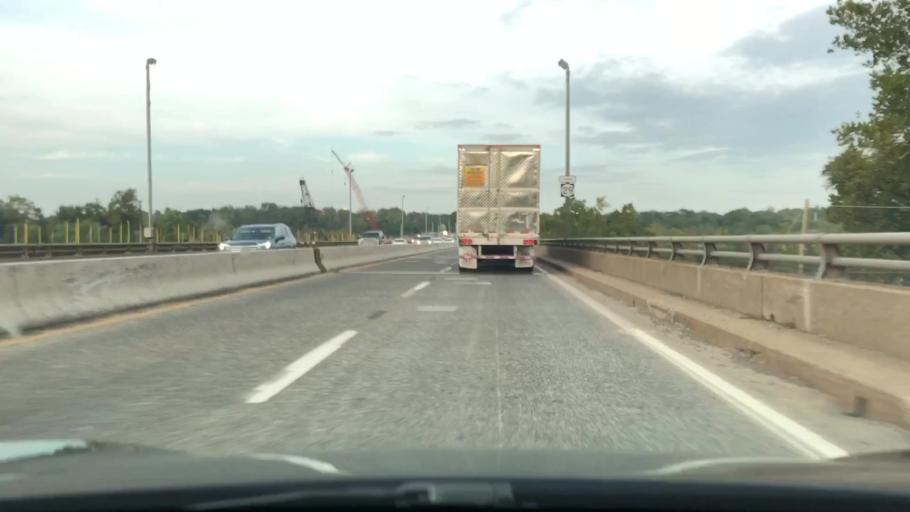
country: US
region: Pennsylvania
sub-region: Bucks County
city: Yardley
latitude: 40.2571
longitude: -74.8499
